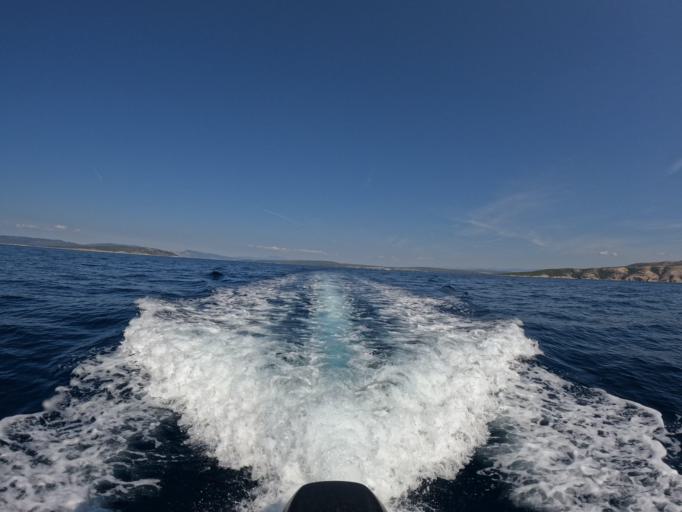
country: HR
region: Primorsko-Goranska
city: Punat
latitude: 44.9464
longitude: 14.6142
